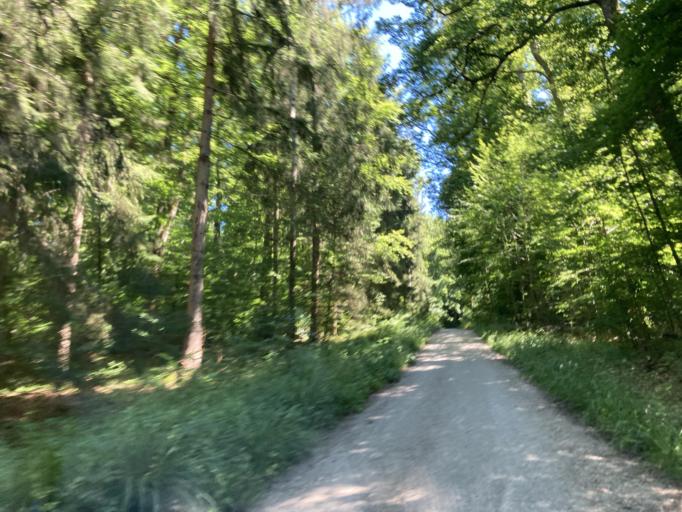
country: DE
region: Baden-Wuerttemberg
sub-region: Tuebingen Region
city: Gomaringen
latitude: 48.4478
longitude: 9.1184
